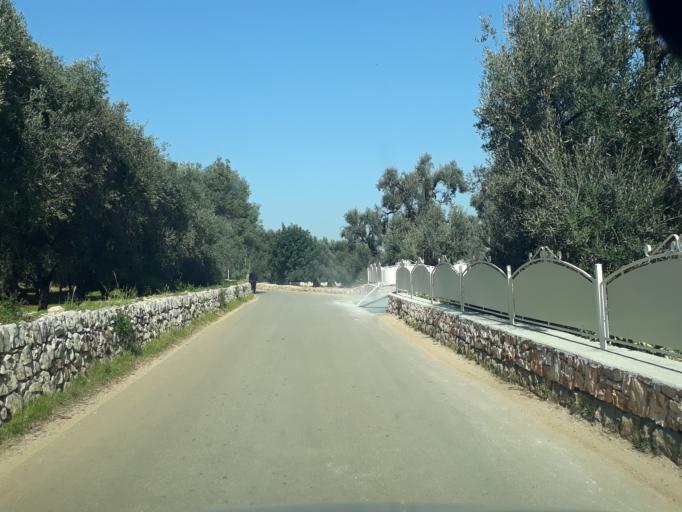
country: IT
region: Apulia
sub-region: Provincia di Brindisi
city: Fasano
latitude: 40.8410
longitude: 17.3459
